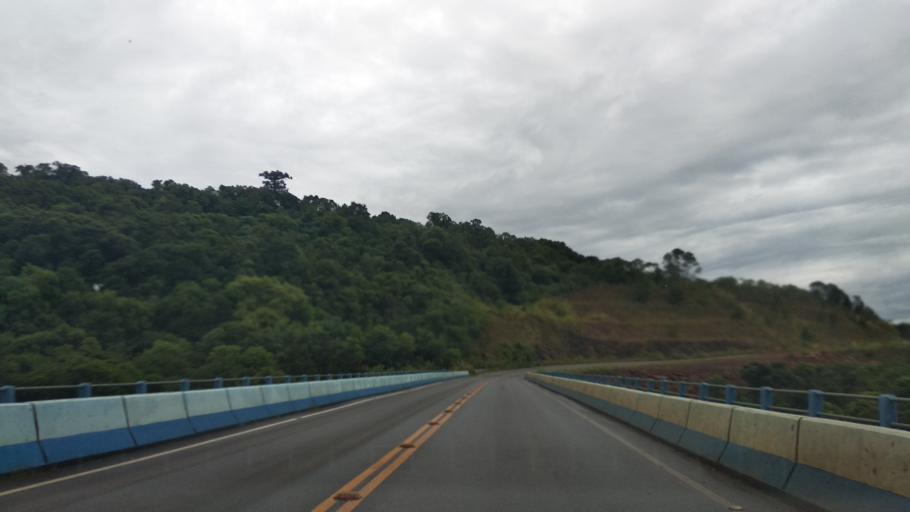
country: BR
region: Santa Catarina
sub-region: Videira
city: Videira
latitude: -27.0026
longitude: -51.1711
